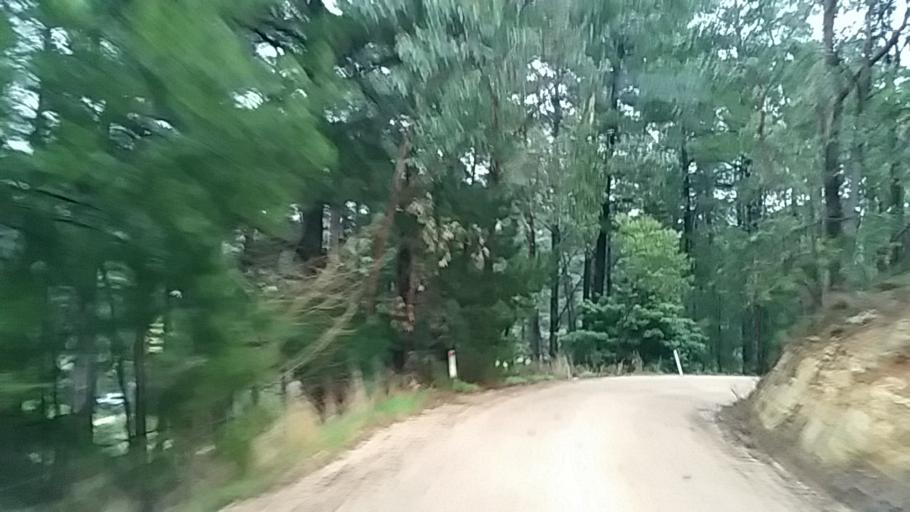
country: AU
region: South Australia
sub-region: Adelaide Hills
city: Adelaide Hills
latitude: -34.9270
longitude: 138.7354
